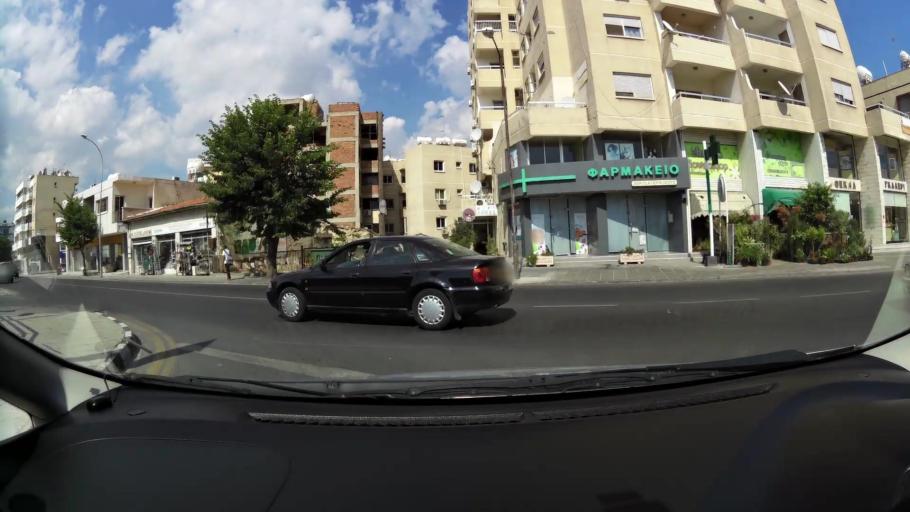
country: CY
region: Larnaka
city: Larnaca
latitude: 34.9187
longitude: 33.6189
